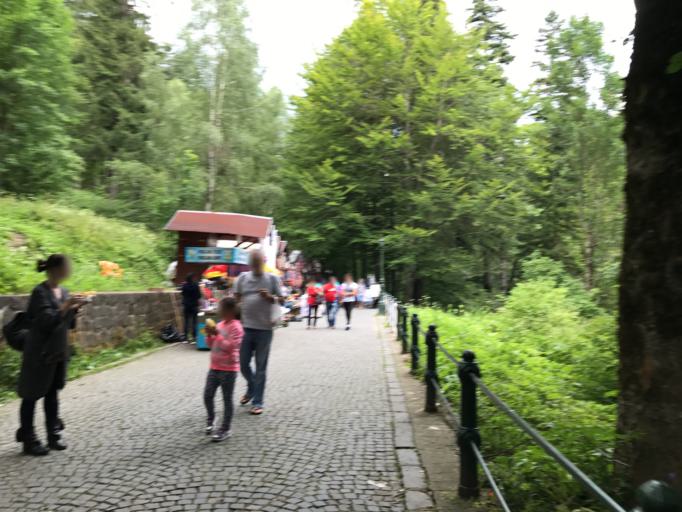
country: RO
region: Prahova
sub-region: Oras Sinaia
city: Sinaia
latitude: 45.3573
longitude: 25.5461
